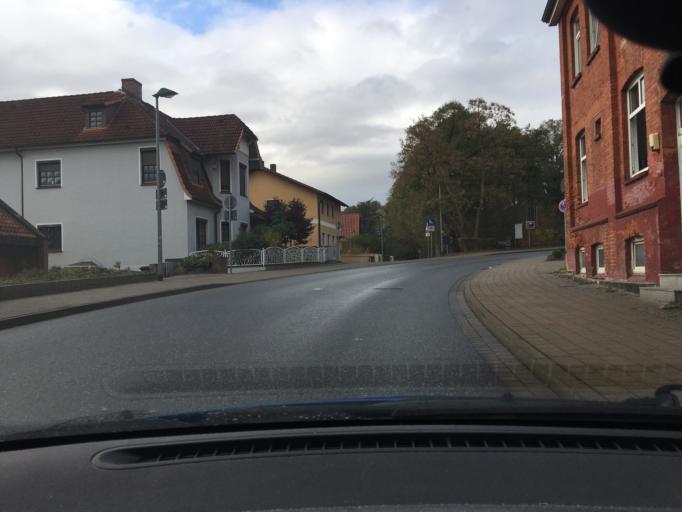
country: DE
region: Schleswig-Holstein
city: Molln
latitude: 53.6329
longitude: 10.6914
